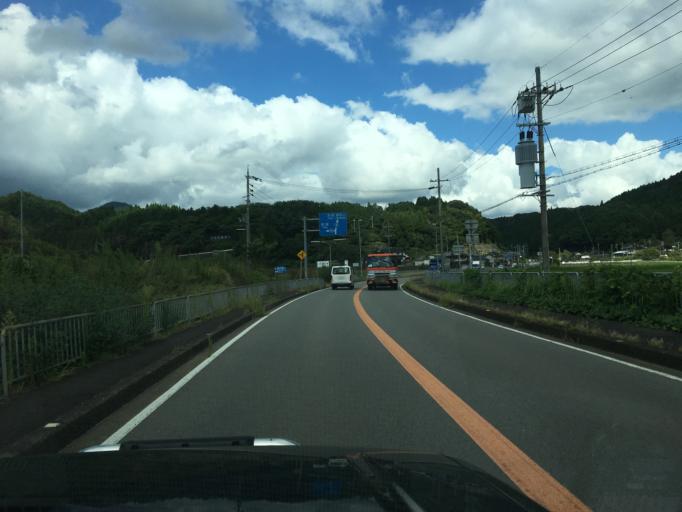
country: JP
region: Kyoto
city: Fukuchiyama
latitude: 35.3284
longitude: 134.9059
